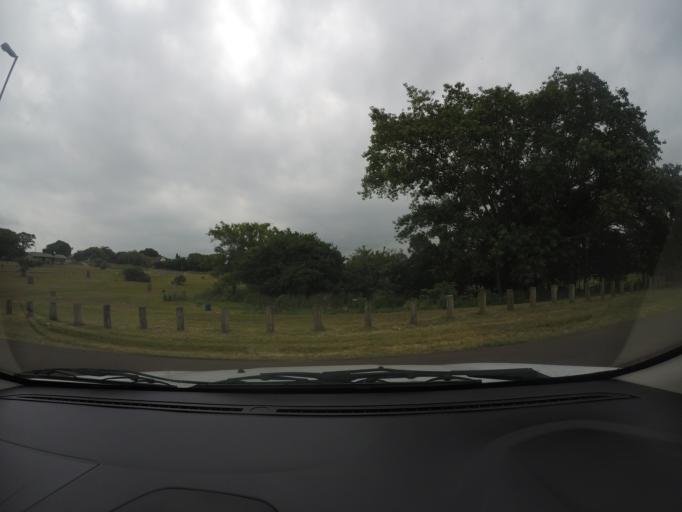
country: ZA
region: KwaZulu-Natal
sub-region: uThungulu District Municipality
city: Empangeni
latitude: -28.7378
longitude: 31.8972
